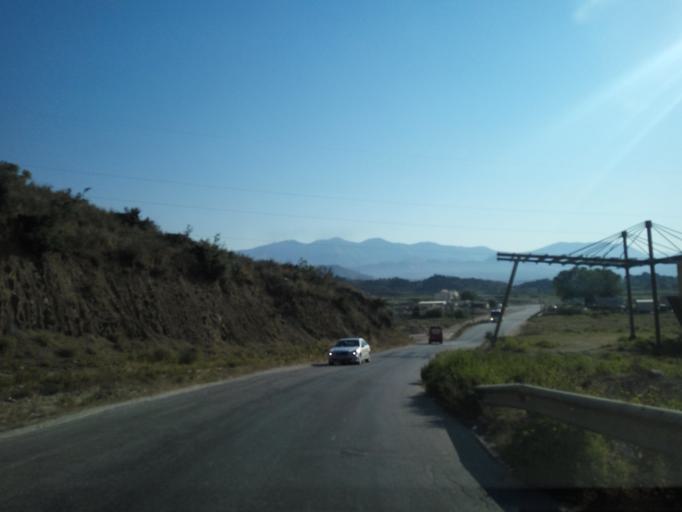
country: AL
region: Vlore
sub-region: Rrethi i Sarandes
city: Sarande
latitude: 39.8789
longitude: 20.0320
